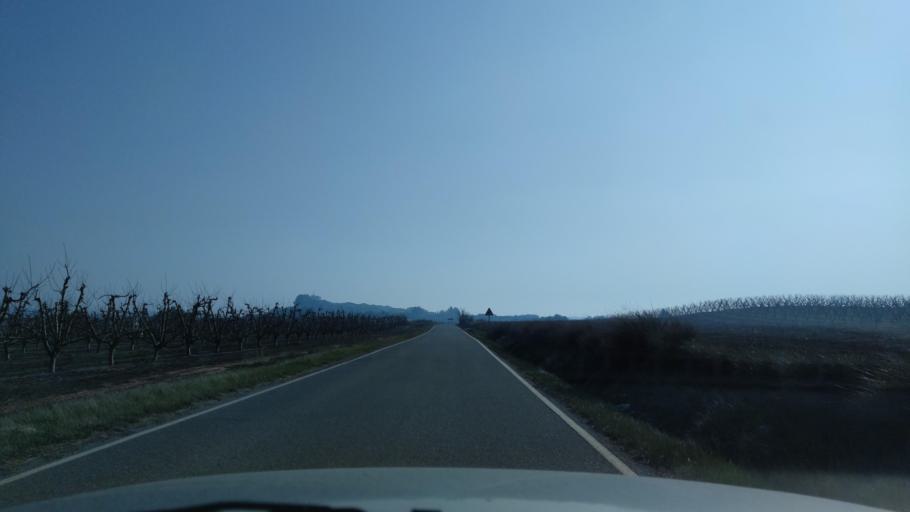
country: ES
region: Catalonia
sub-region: Provincia de Lleida
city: Sunyer
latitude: 41.5283
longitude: 0.5830
